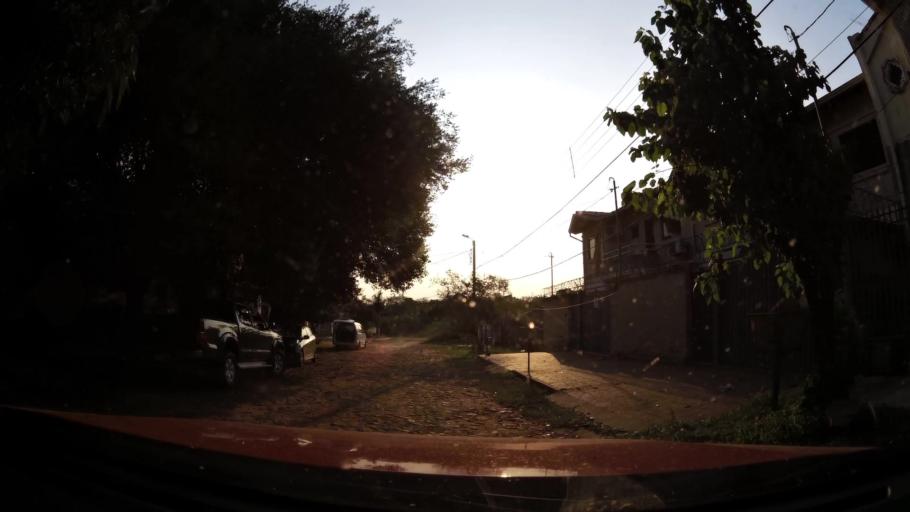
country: PY
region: Central
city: Lambare
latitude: -25.3454
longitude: -57.6030
